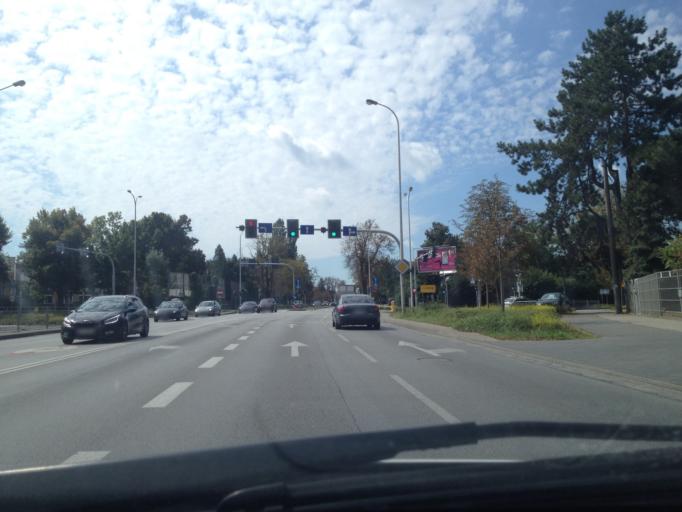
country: PL
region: Lower Silesian Voivodeship
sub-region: Powiat wroclawski
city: Wroclaw
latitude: 51.0714
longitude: 17.0111
